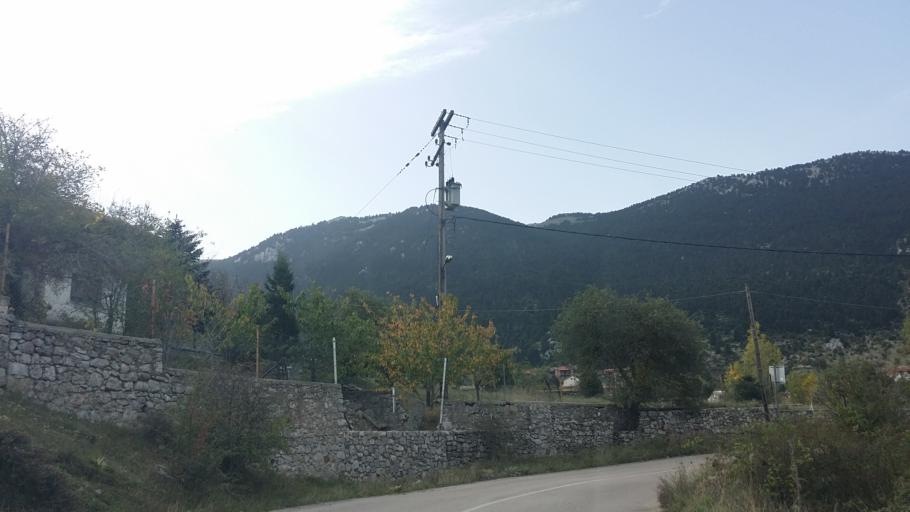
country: GR
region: Central Greece
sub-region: Nomos Voiotias
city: Kyriaki
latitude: 38.3688
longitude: 22.8448
